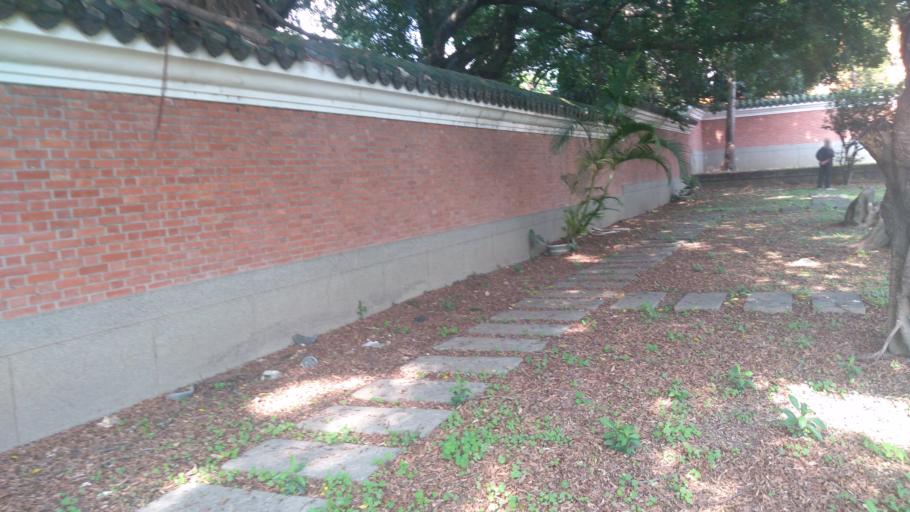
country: TW
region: Taiwan
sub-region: Taichung City
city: Taichung
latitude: 24.1535
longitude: 120.6906
